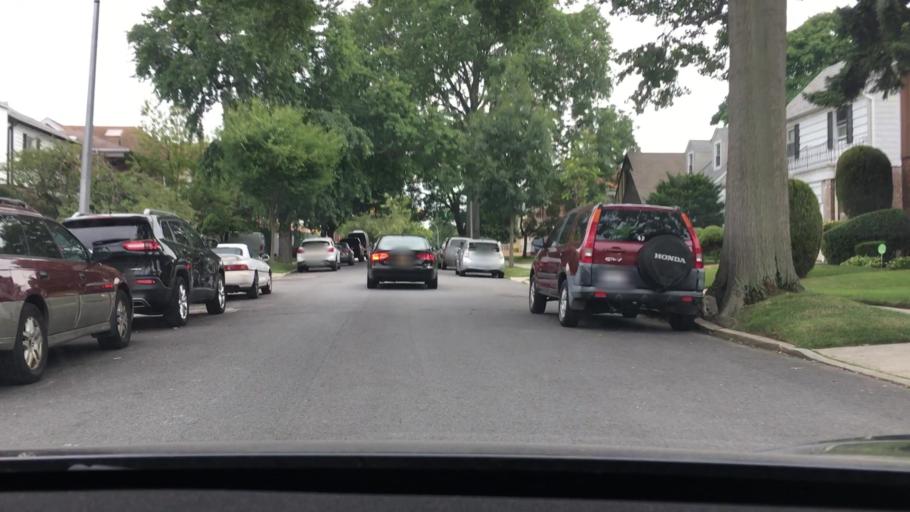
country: US
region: New York
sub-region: Queens County
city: Jamaica
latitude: 40.7332
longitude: -73.7860
